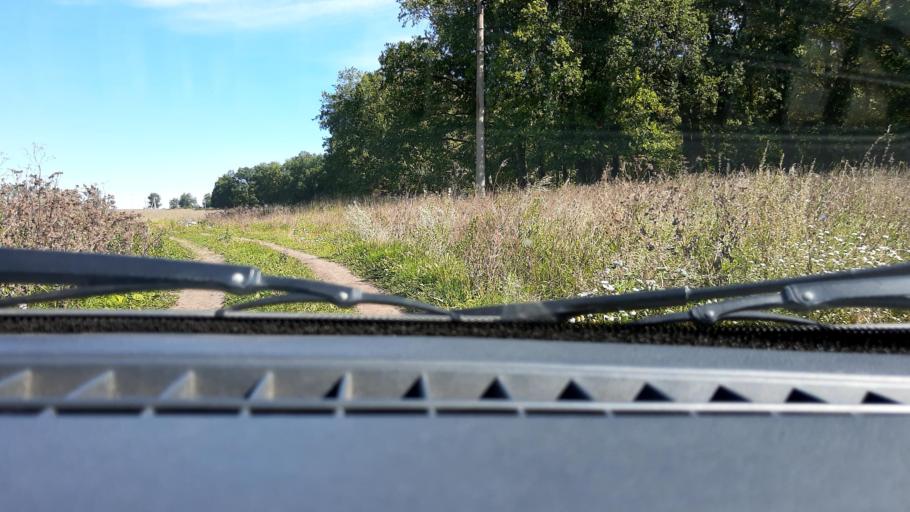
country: RU
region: Bashkortostan
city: Mikhaylovka
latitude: 54.8225
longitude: 55.7917
